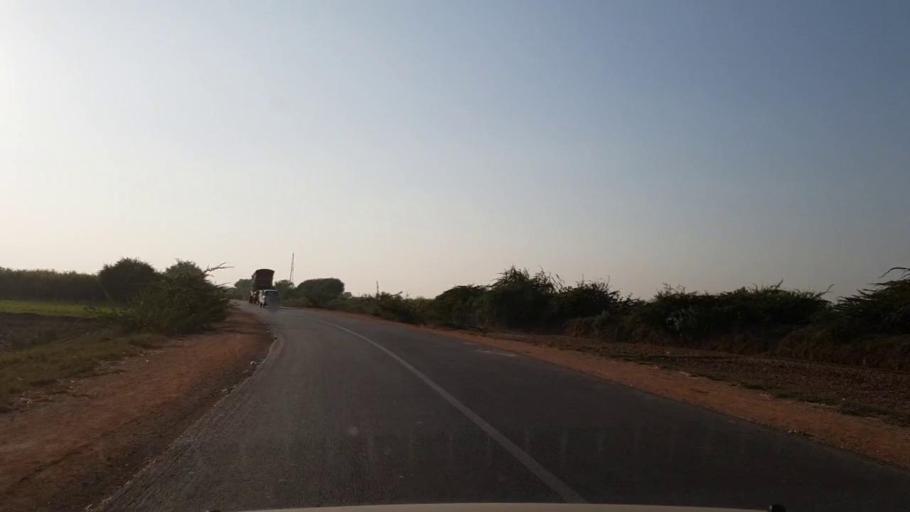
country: PK
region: Sindh
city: Mirpur Batoro
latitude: 24.6874
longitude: 68.1730
